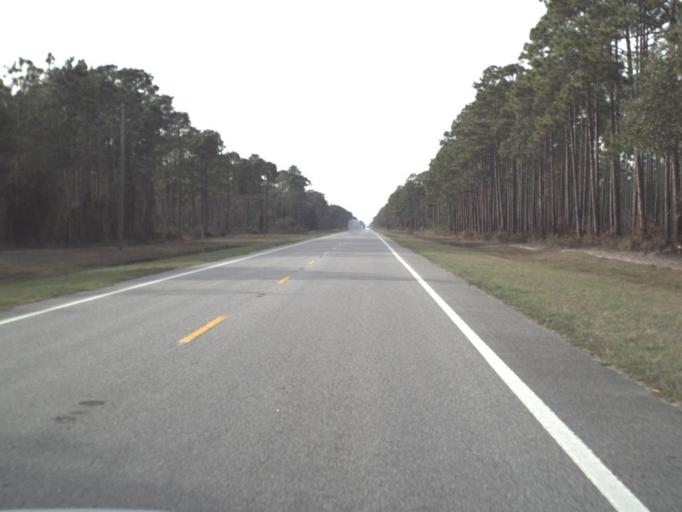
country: US
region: Florida
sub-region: Bay County
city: Mexico Beach
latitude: 30.0034
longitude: -85.5038
